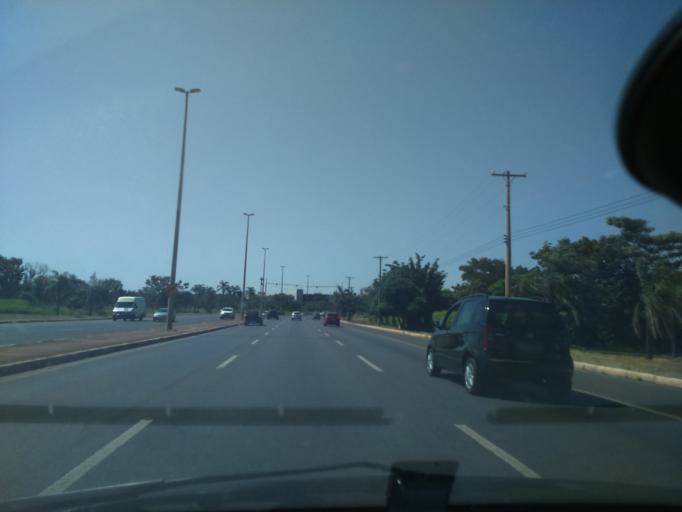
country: BR
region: Federal District
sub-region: Brasilia
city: Brasilia
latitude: -15.8081
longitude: -47.8501
